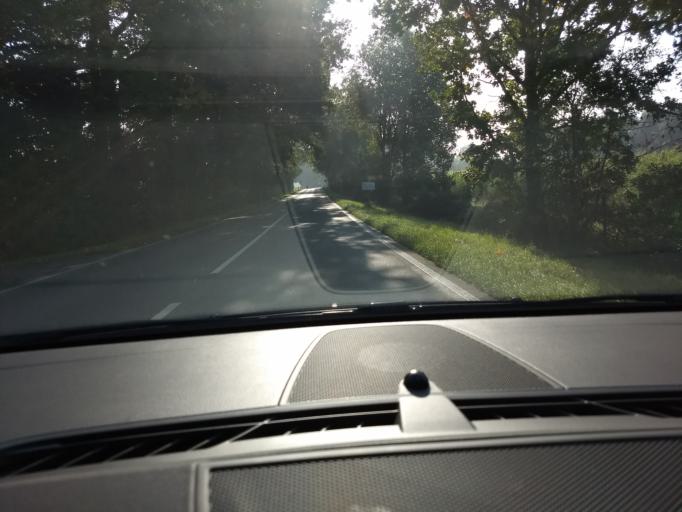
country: DE
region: North Rhine-Westphalia
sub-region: Regierungsbezirk Munster
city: Heiden
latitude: 51.8425
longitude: 6.9055
